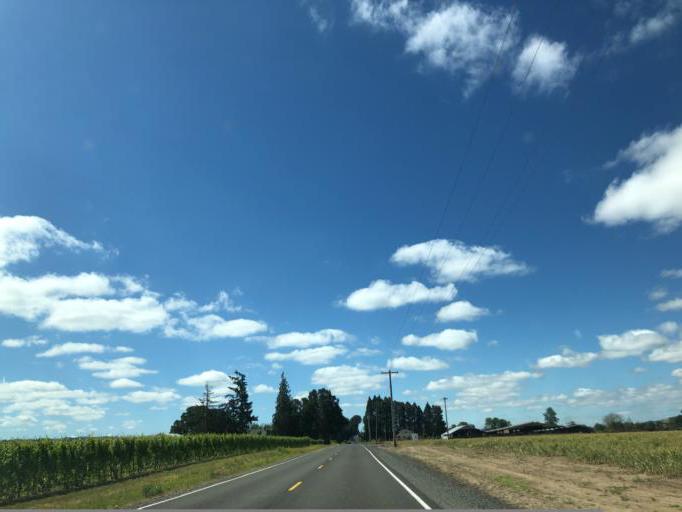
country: US
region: Oregon
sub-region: Marion County
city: Mount Angel
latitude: 45.0782
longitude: -122.7435
